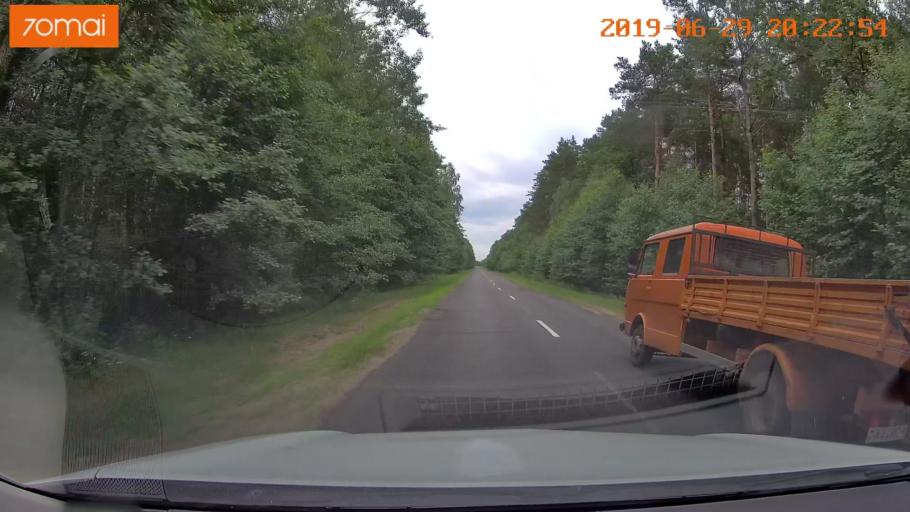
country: BY
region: Brest
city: Asnyezhytsy
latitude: 52.4376
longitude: 26.2573
